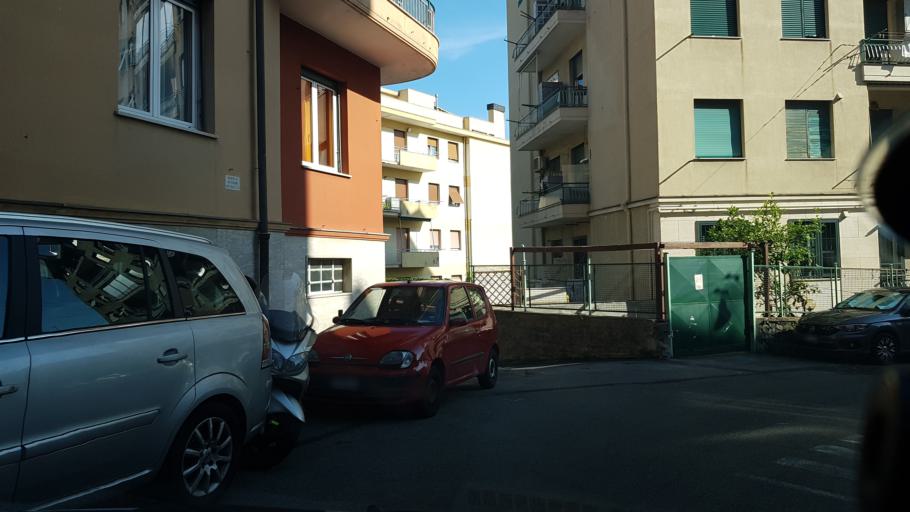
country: IT
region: Liguria
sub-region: Provincia di Genova
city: Genoa
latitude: 44.4393
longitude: 8.8961
